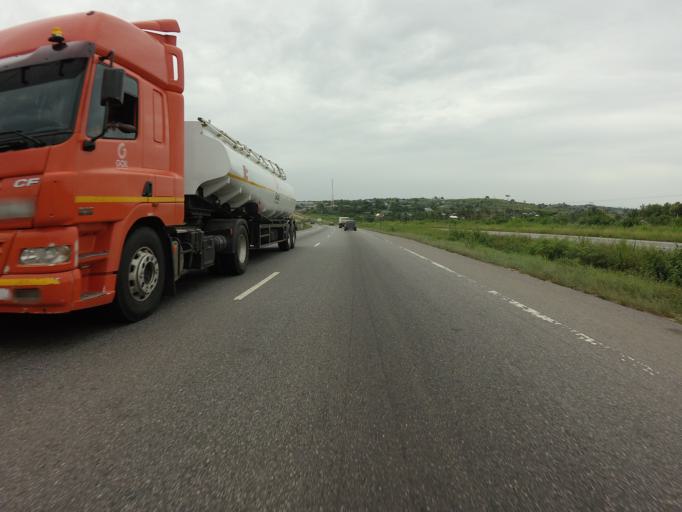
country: GH
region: Eastern
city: Nsawam
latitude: 5.8569
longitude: -0.3590
